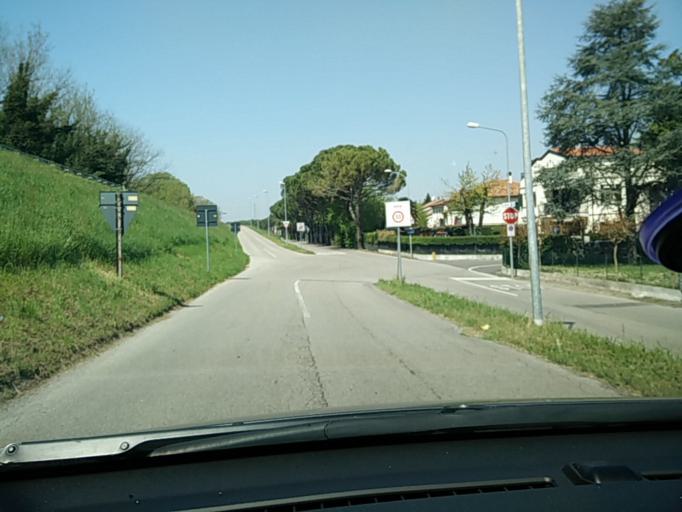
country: IT
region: Veneto
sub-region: Provincia di Venezia
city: San Dona di Piave
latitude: 45.6305
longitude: 12.5579
